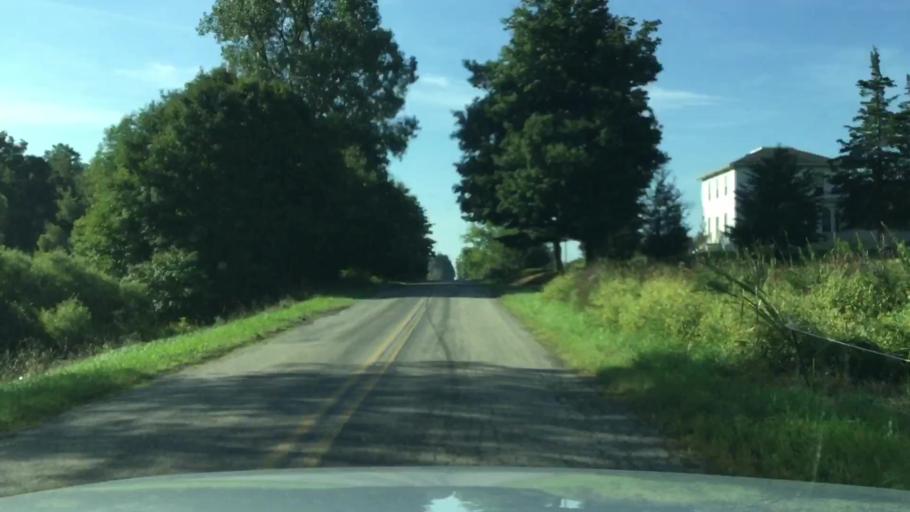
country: US
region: Michigan
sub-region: Lenawee County
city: Hudson
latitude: 41.8932
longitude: -84.4203
